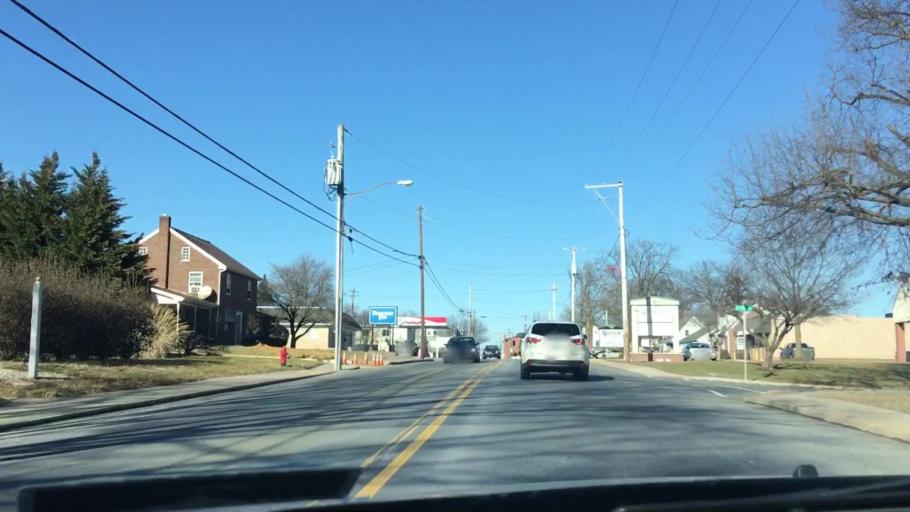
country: US
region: Pennsylvania
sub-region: Lancaster County
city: Akron
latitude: 40.1544
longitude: -76.2062
